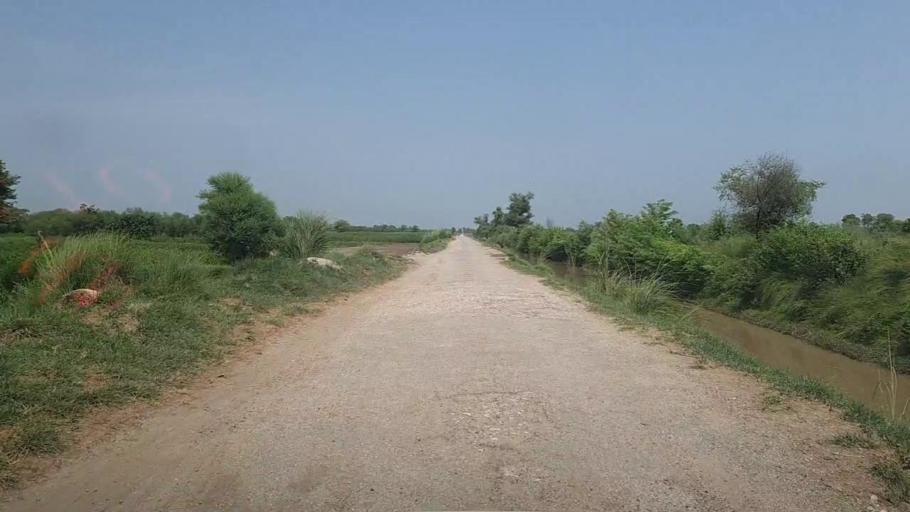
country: PK
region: Sindh
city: Karaundi
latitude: 26.8775
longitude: 68.3358
